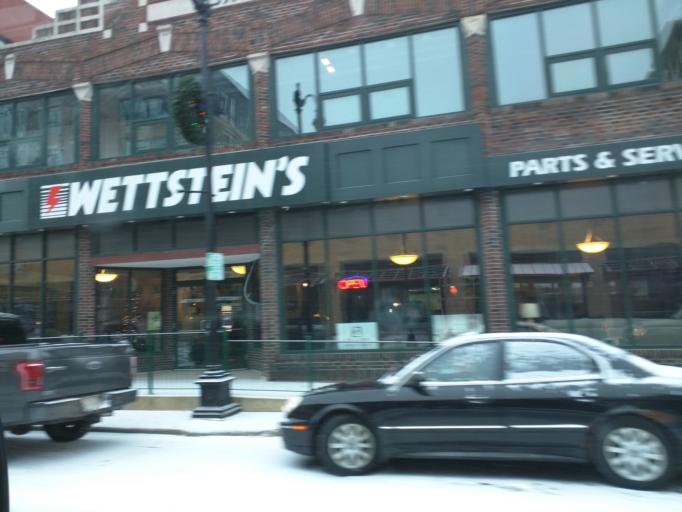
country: US
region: Wisconsin
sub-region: La Crosse County
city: La Crosse
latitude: 43.8142
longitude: -91.2516
